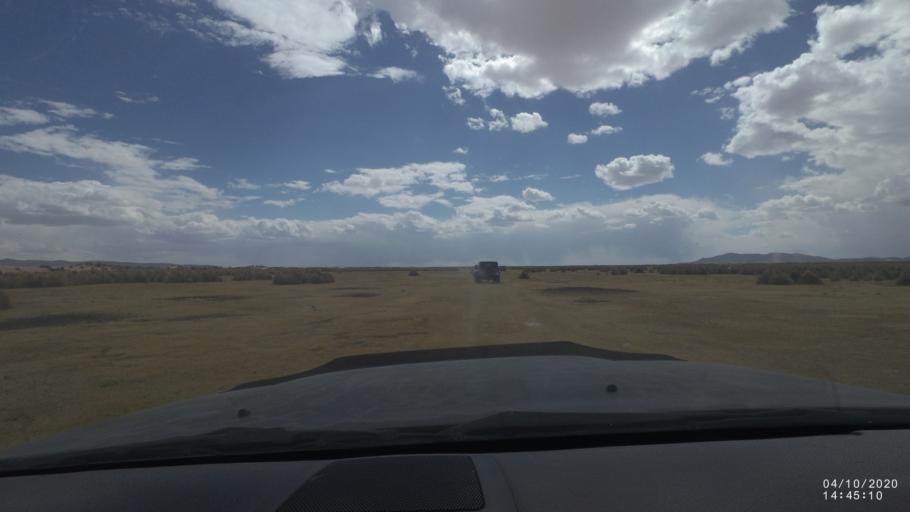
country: BO
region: Oruro
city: Poopo
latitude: -18.6865
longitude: -67.4979
